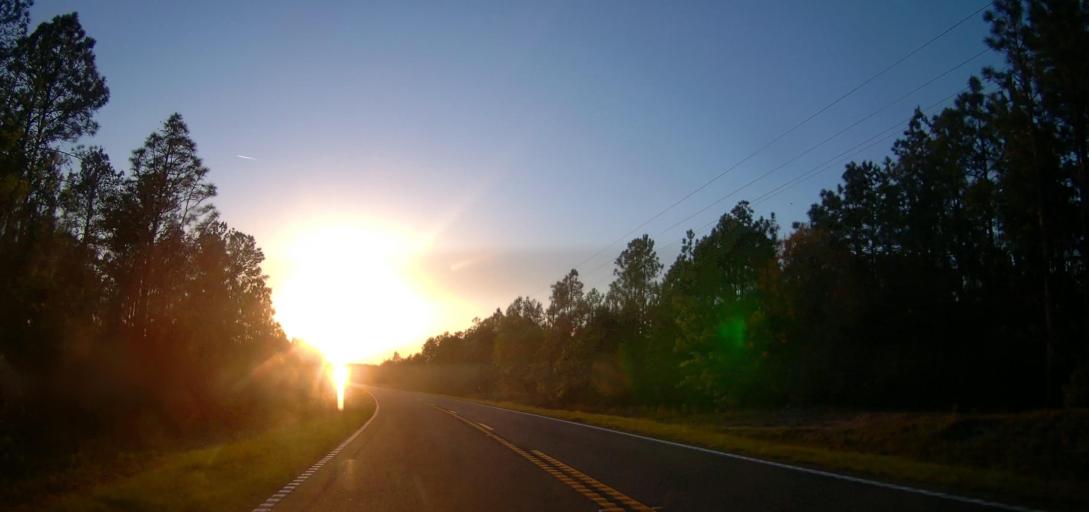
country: US
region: Georgia
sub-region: Marion County
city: Buena Vista
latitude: 32.4414
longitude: -84.6049
